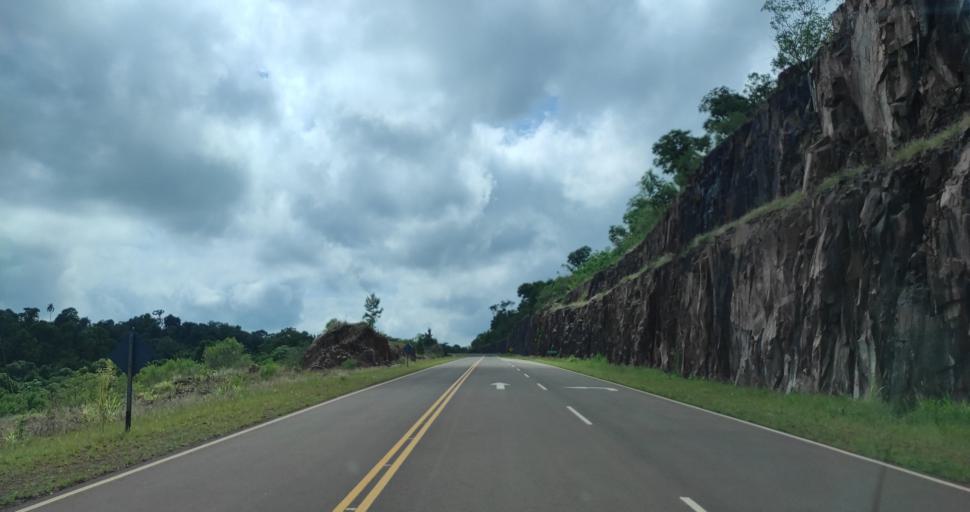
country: AR
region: Misiones
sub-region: Departamento de Veinticinco de Mayo
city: Veinticinco de Mayo
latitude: -27.3842
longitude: -54.8017
